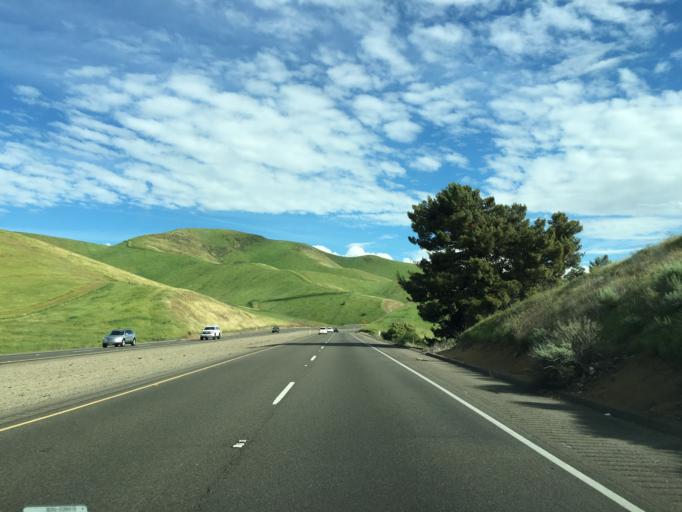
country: US
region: California
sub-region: Merced County
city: Gustine
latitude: 37.1034
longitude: -121.1264
